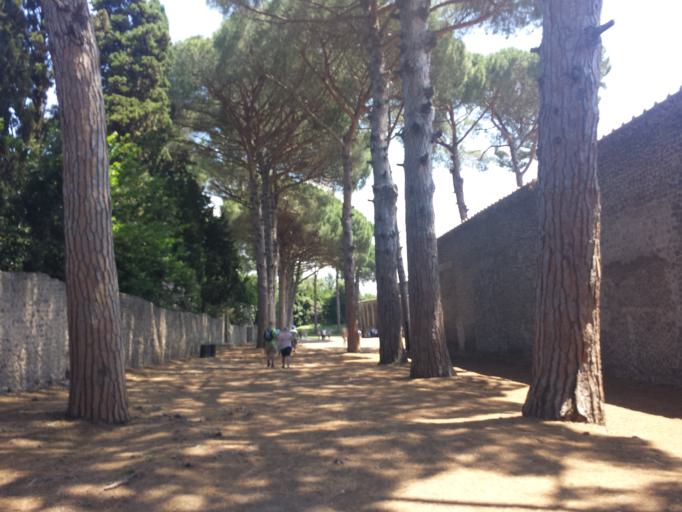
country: IT
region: Campania
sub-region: Provincia di Napoli
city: Pompei
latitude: 40.7514
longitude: 14.4935
